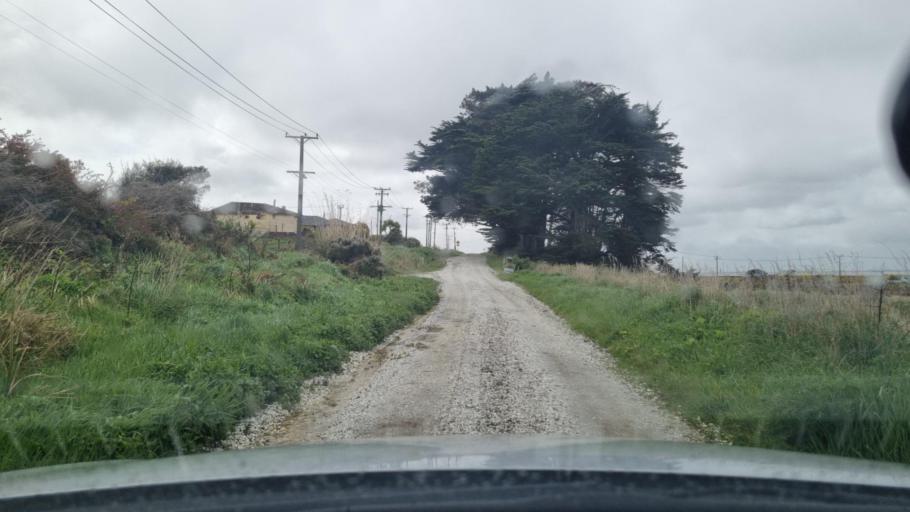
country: NZ
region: Southland
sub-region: Invercargill City
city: Bluff
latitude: -46.5865
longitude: 168.3026
